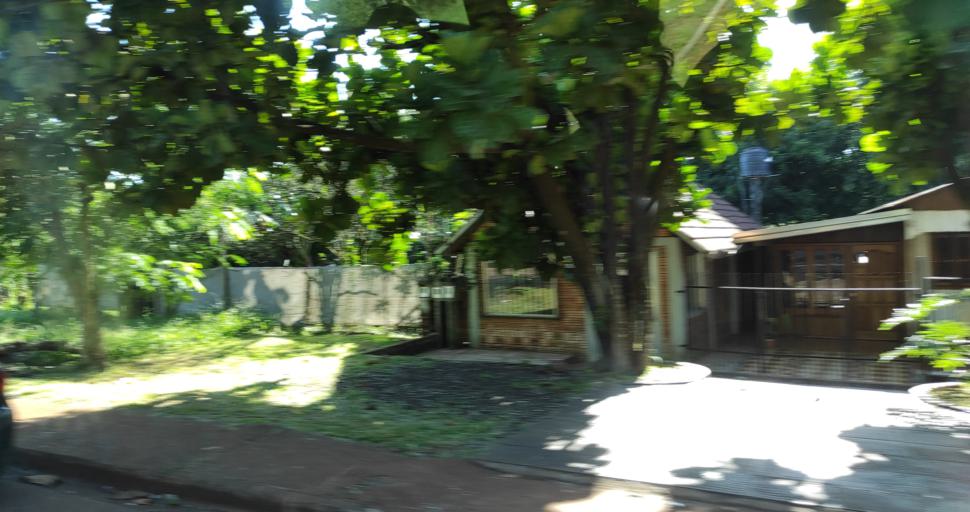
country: AR
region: Misiones
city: El Soberbio
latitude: -27.2931
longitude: -54.1982
